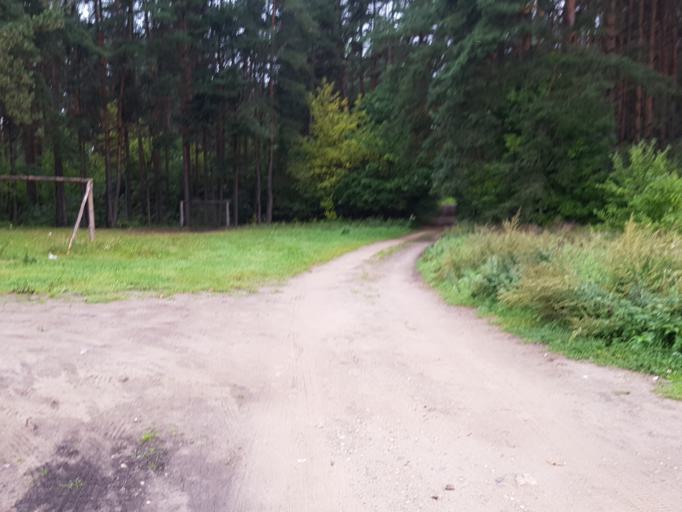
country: LT
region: Vilnius County
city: Lazdynai
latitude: 54.6507
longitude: 25.2056
